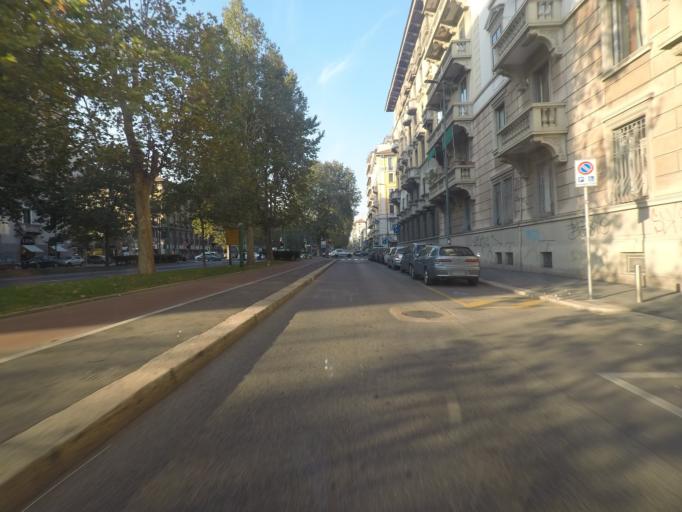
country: IT
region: Lombardy
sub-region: Citta metropolitana di Milano
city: Milano
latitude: 45.4615
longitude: 9.2242
